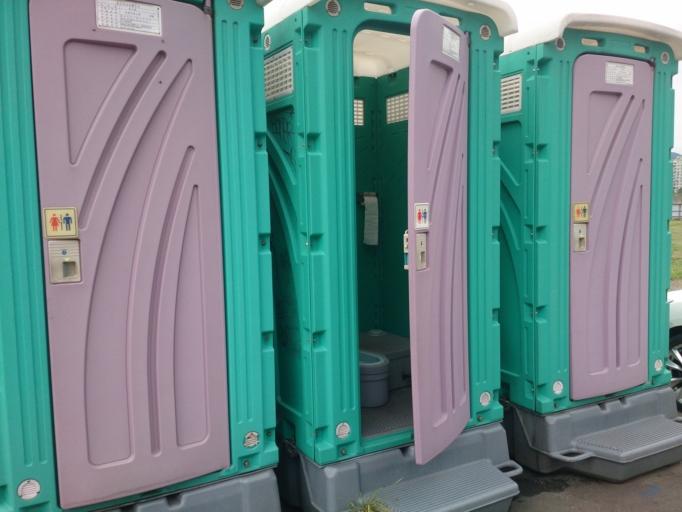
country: TW
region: Taipei
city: Taipei
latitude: 25.0736
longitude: 121.5532
